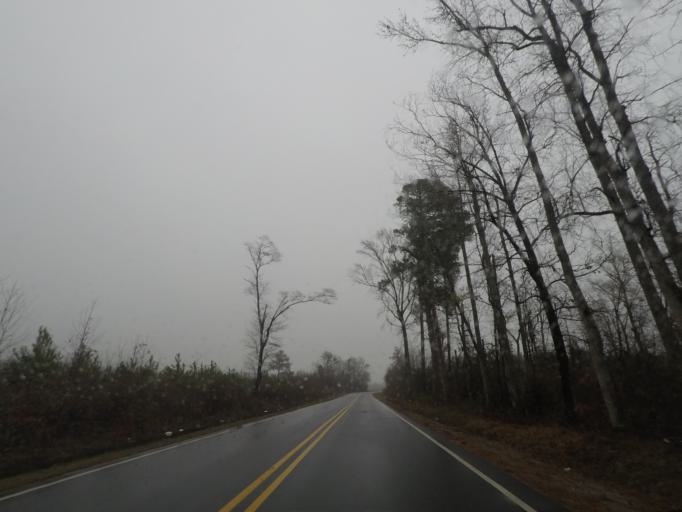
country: US
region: North Carolina
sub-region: Scotland County
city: Laurinburg
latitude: 34.8096
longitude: -79.4445
